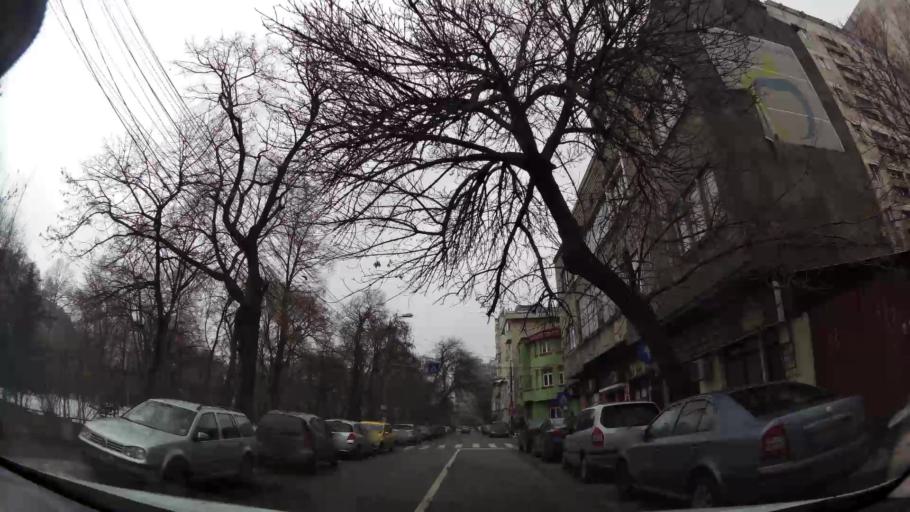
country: RO
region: Bucuresti
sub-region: Municipiul Bucuresti
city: Bucuresti
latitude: 44.4581
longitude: 26.0645
